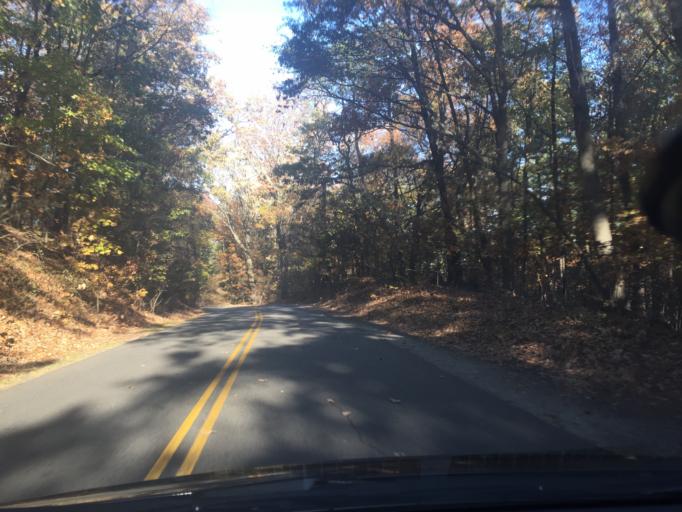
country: US
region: Georgia
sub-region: Cobb County
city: Marietta
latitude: 33.9820
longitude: -84.5738
